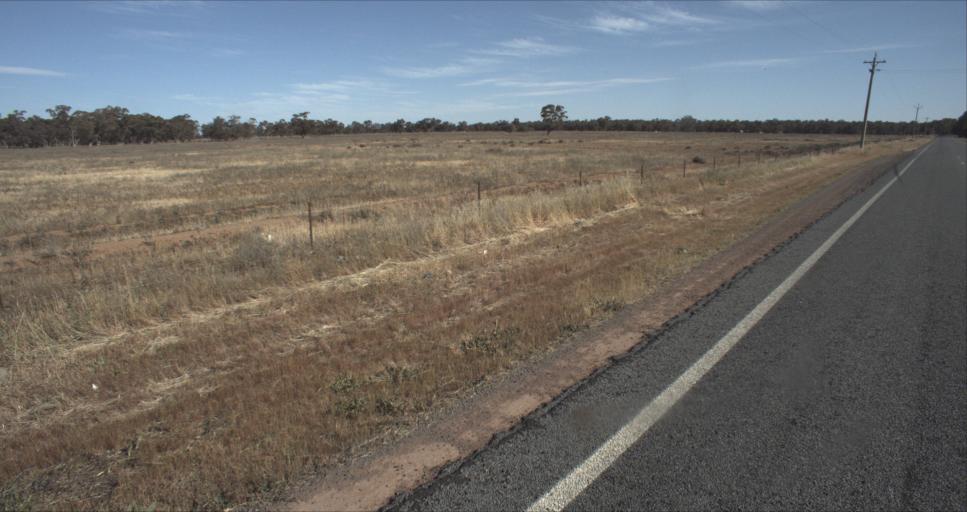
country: AU
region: New South Wales
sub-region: Leeton
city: Leeton
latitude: -34.6167
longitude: 146.4003
